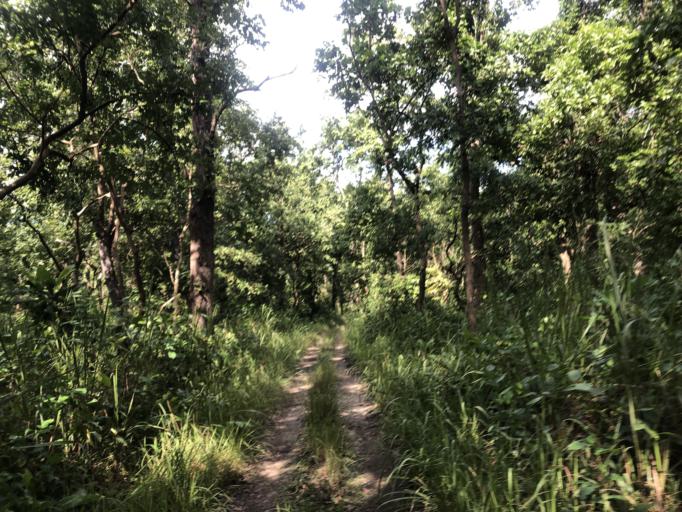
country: NP
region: Far Western
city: Tikapur
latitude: 28.5578
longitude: 81.2934
